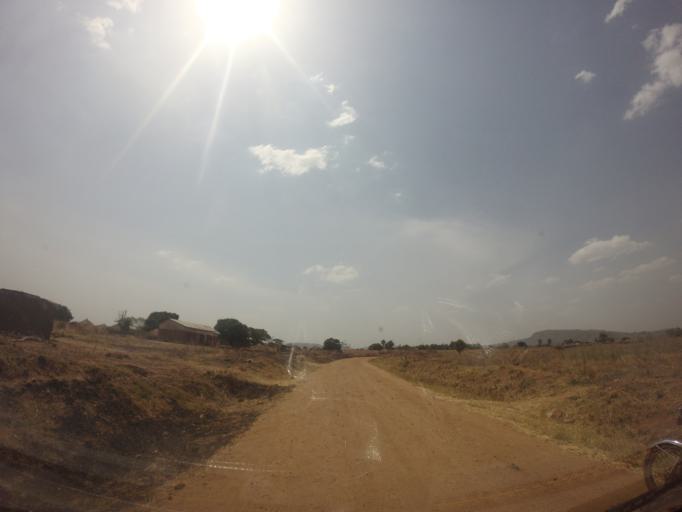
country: UG
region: Northern Region
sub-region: Arua District
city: Arua
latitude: 2.9083
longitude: 31.0558
